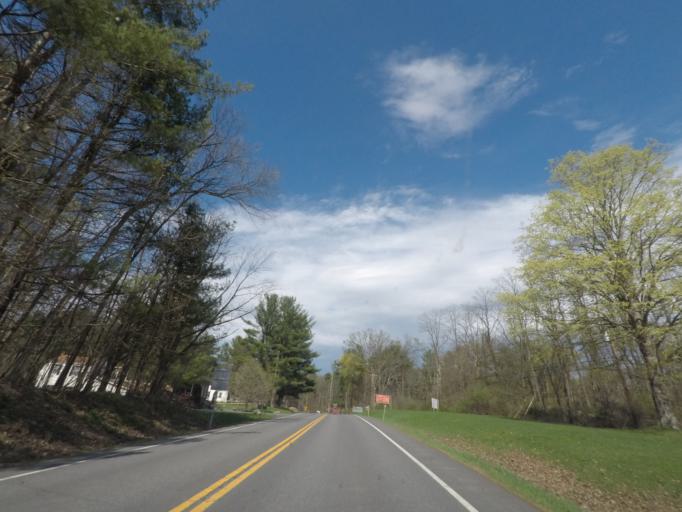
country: US
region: New York
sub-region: Greene County
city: Cairo
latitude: 42.3624
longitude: -74.0447
